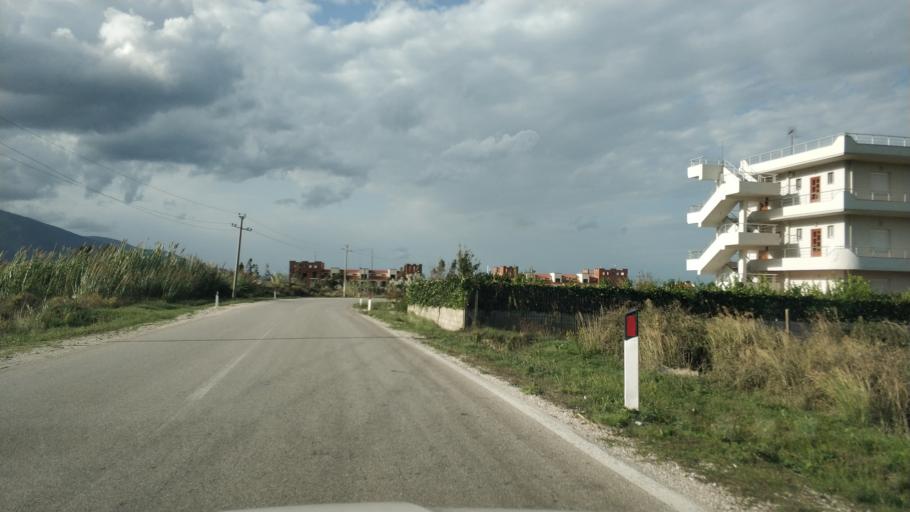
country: AL
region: Vlore
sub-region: Rrethi i Vlores
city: Orikum
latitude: 40.3365
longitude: 19.4761
